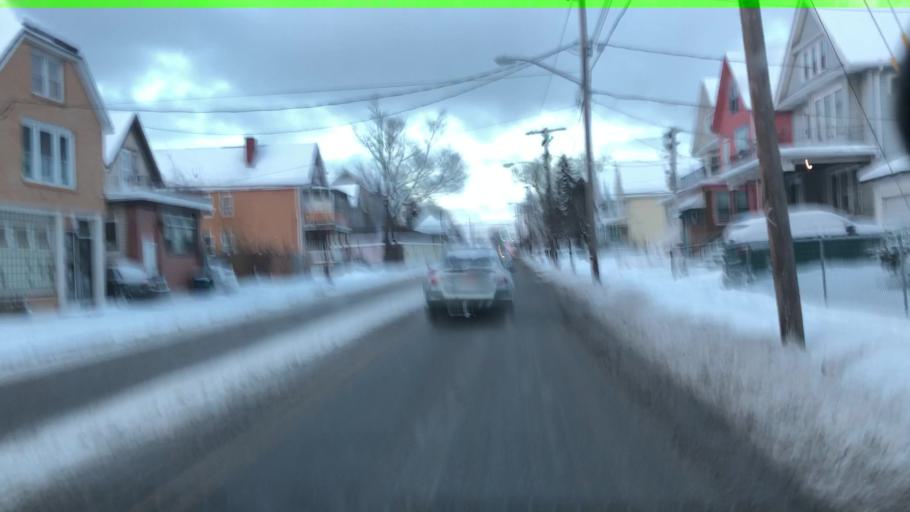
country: US
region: New York
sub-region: Erie County
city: Buffalo
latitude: 42.9038
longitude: -78.8473
